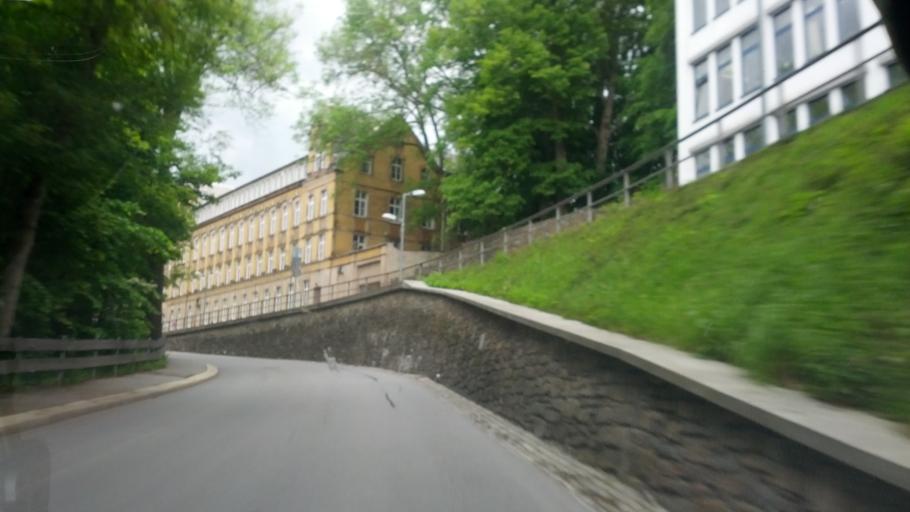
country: DE
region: Saxony
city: Annaberg-Buchholz
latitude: 50.5721
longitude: 13.0000
